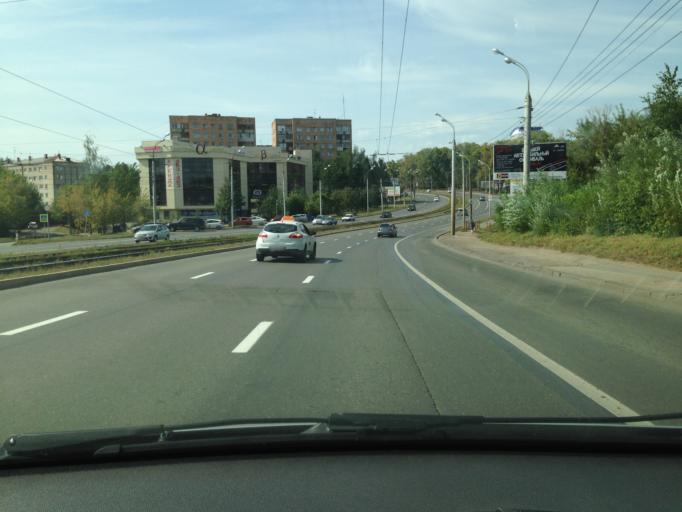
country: RU
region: Udmurtiya
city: Izhevsk
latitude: 56.8605
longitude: 53.1919
